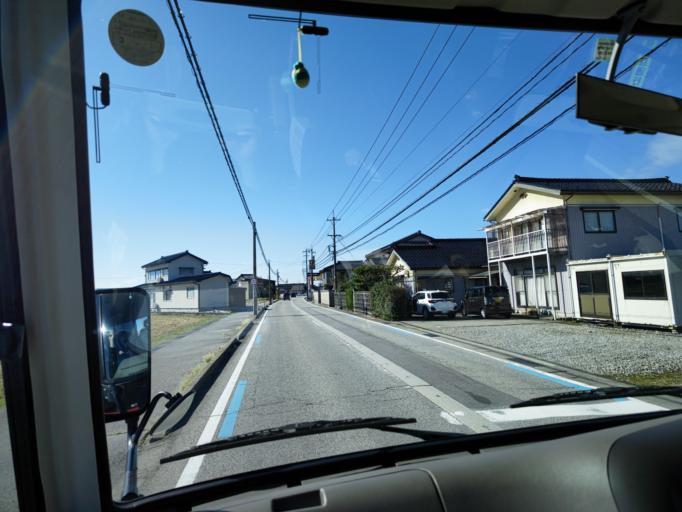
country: JP
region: Toyama
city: Nyuzen
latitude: 36.8992
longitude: 137.4210
